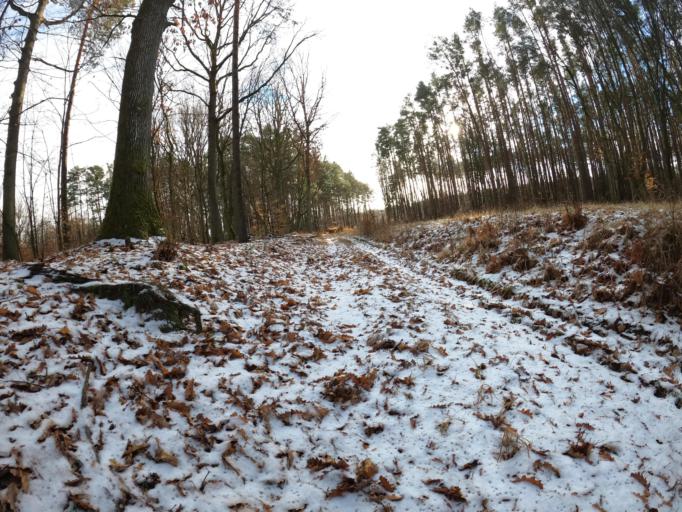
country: PL
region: Lubusz
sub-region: Powiat slubicki
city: Rzepin
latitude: 52.2960
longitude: 14.8144
